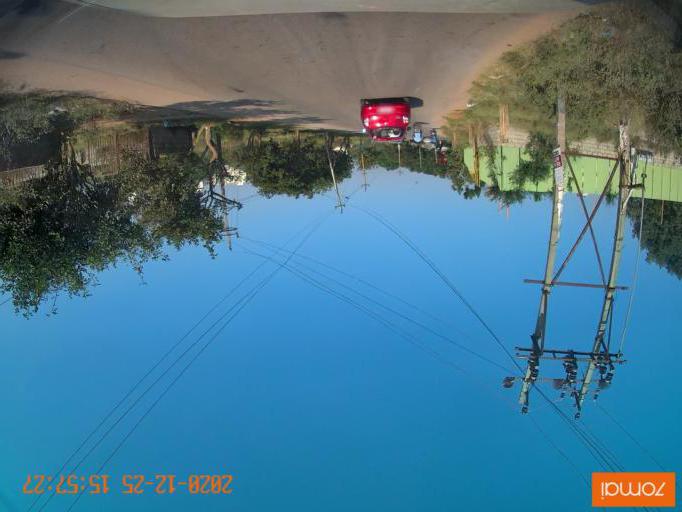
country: IN
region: Karnataka
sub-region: Bangalore Urban
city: Bangalore
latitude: 12.8696
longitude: 77.6228
